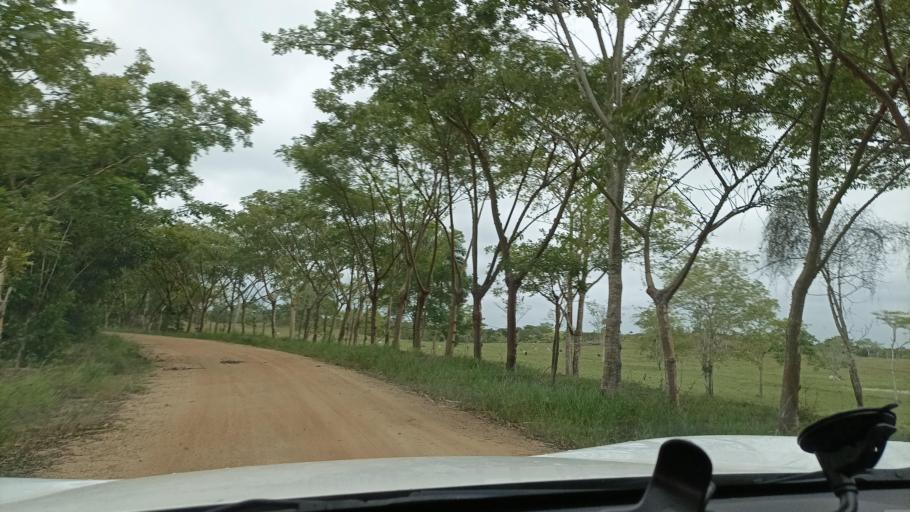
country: MX
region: Veracruz
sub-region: Moloacan
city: Cuichapa
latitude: 17.7918
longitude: -94.3699
